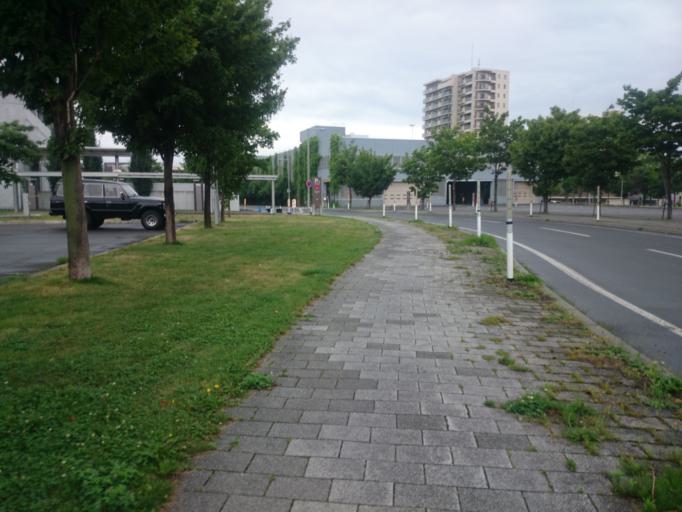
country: JP
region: Hokkaido
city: Sapporo
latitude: 43.0579
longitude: 141.3882
